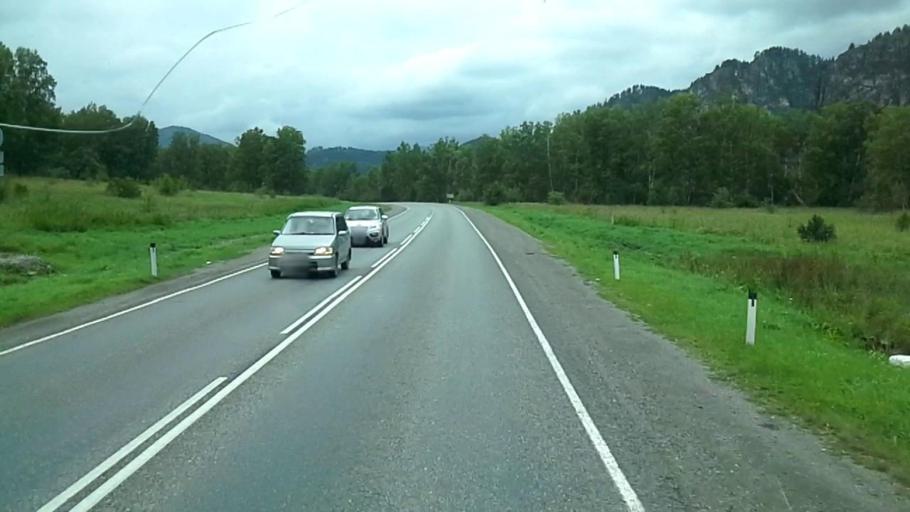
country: RU
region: Altay
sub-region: Mayminskiy Rayon
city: Manzherok
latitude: 51.8554
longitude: 85.7485
